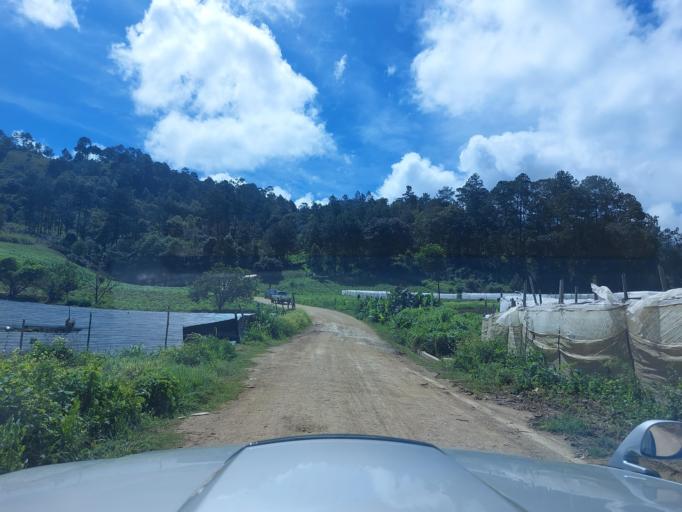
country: GT
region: Chimaltenango
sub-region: Municipio de San Juan Comalapa
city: Comalapa
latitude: 14.7527
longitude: -90.8692
